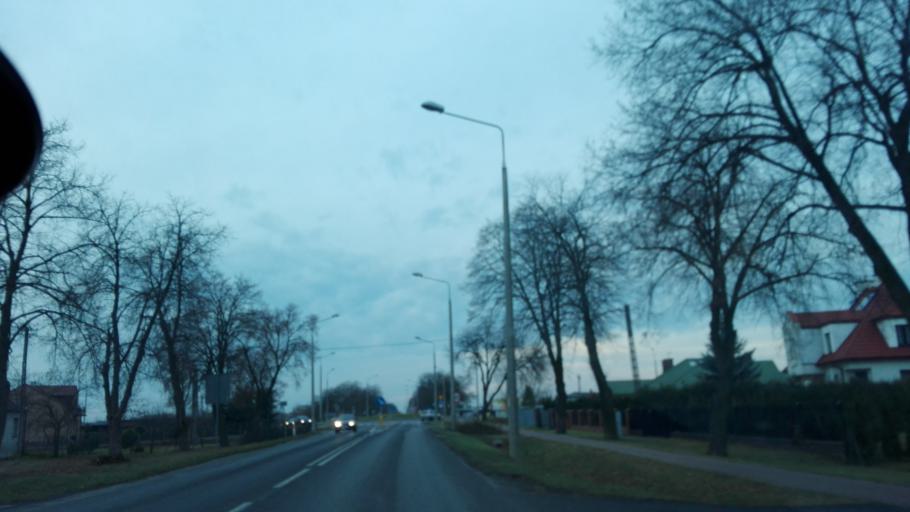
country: PL
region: Lublin Voivodeship
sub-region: Powiat radzynski
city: Radzyn Podlaski
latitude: 51.7740
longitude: 22.6231
